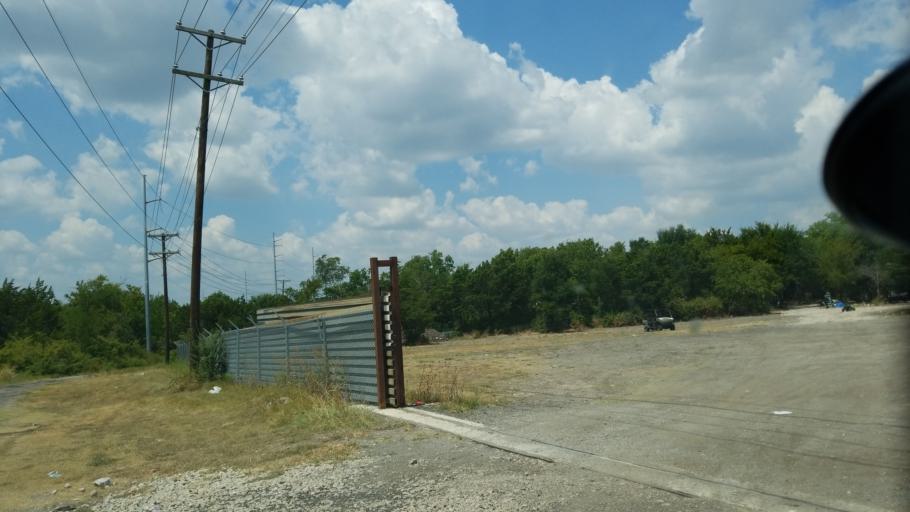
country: US
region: Texas
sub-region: Dallas County
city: Duncanville
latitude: 32.6785
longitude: -96.8853
